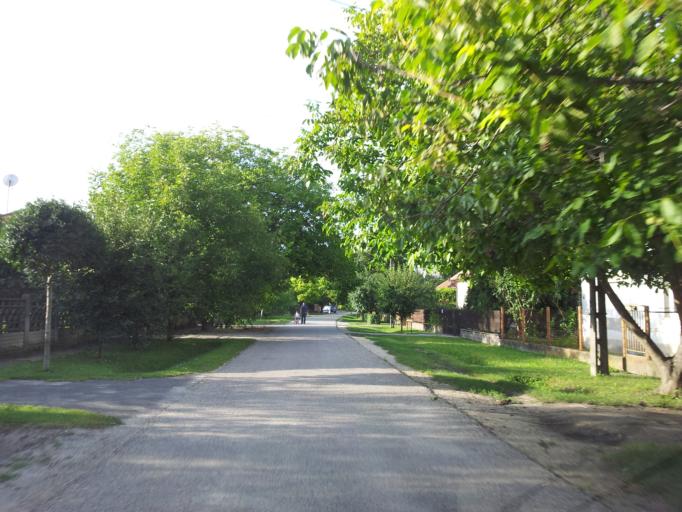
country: HU
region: Pest
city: Kiskunlachaza
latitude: 47.1811
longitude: 19.0086
